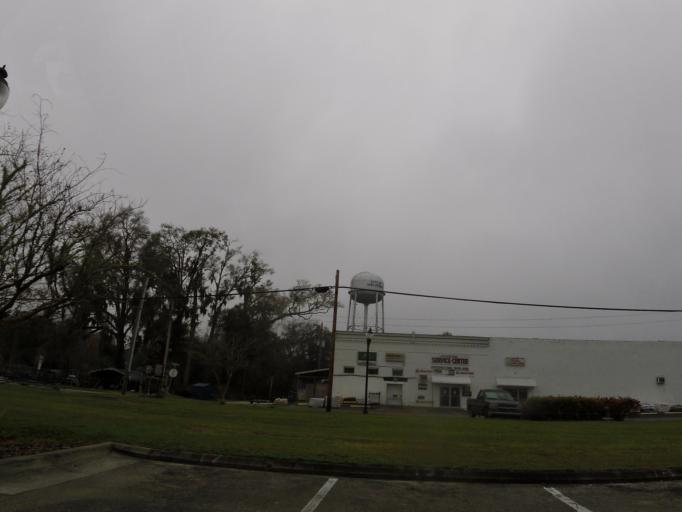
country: US
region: Florida
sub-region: Alachua County
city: High Springs
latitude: 29.8259
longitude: -82.5970
